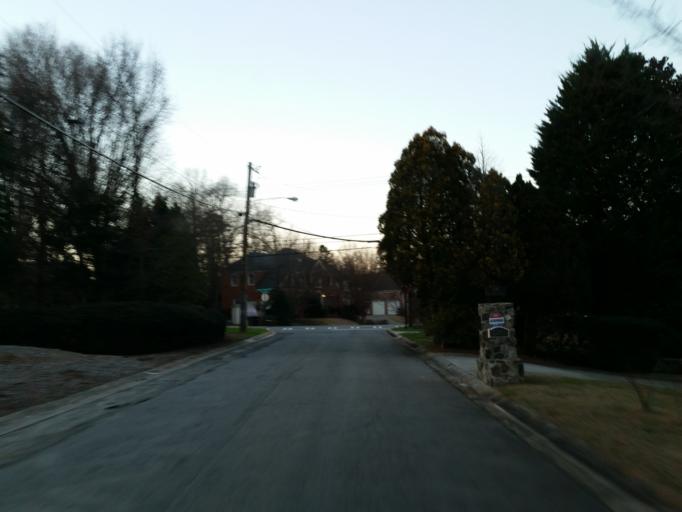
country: US
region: Georgia
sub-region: Fulton County
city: Sandy Springs
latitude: 33.9694
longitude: -84.3979
